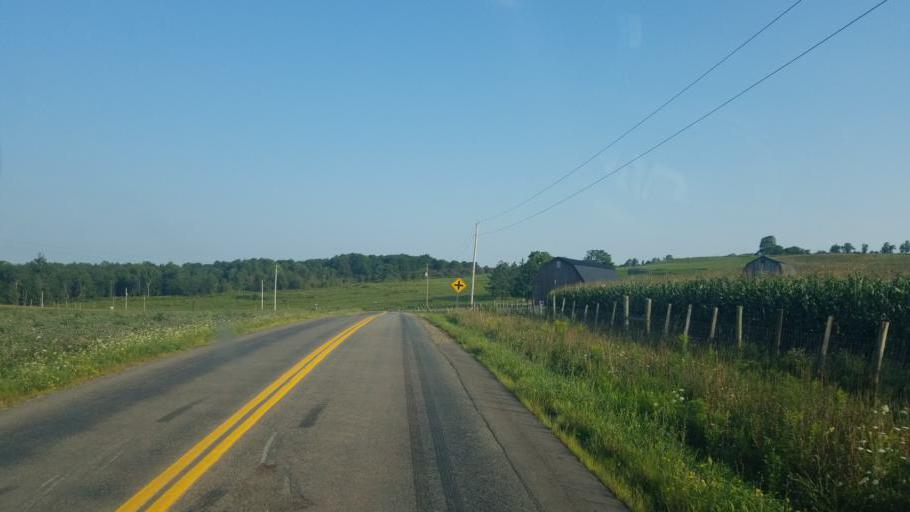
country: US
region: New York
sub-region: Allegany County
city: Andover
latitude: 42.0728
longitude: -77.6371
